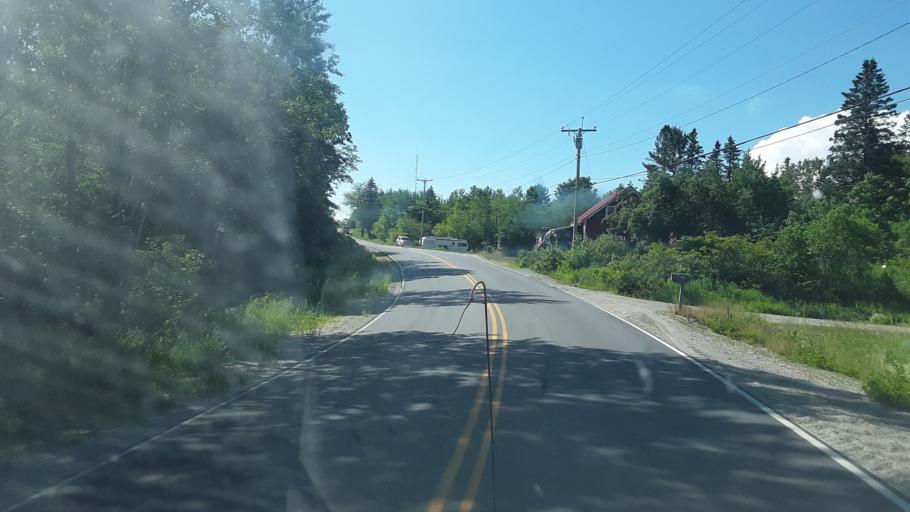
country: US
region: Maine
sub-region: Washington County
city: Cherryfield
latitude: 44.6171
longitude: -67.9257
